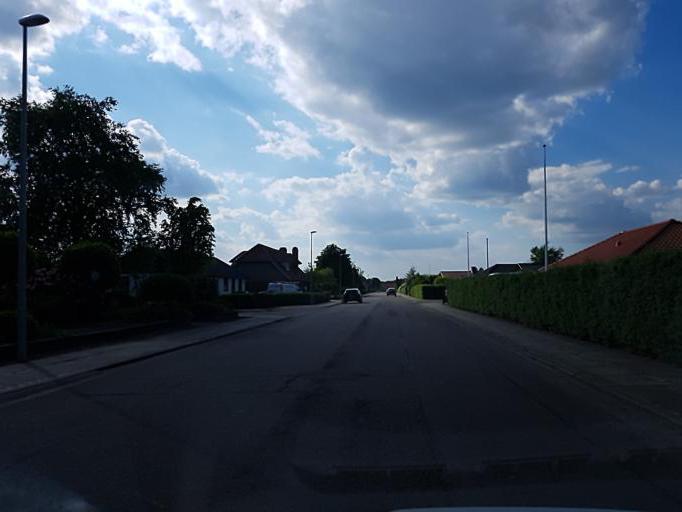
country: DK
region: South Denmark
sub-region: Varde Kommune
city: Varde
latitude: 55.5868
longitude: 8.4235
